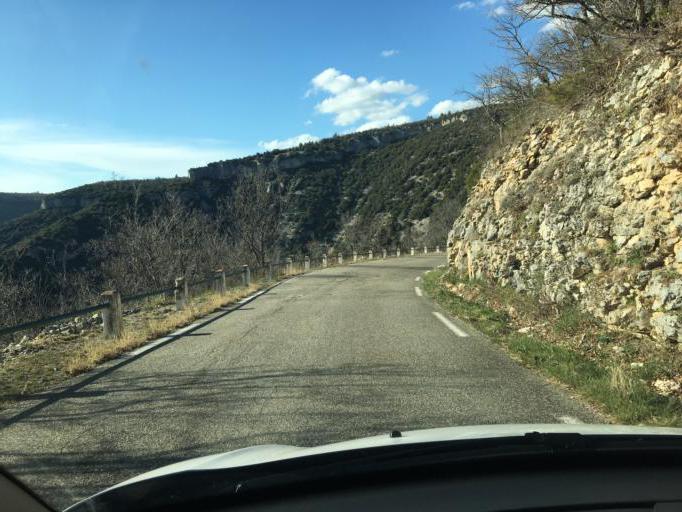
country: FR
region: Provence-Alpes-Cote d'Azur
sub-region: Departement du Vaucluse
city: Villes-sur-Auzon
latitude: 44.0626
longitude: 5.3201
